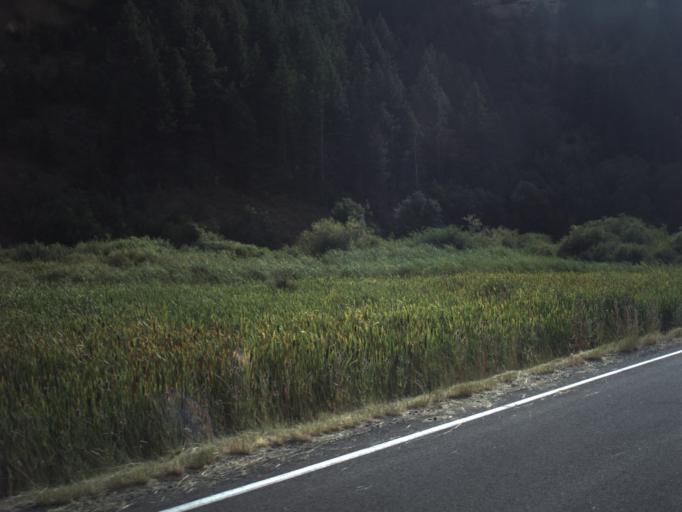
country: US
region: Utah
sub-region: Cache County
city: Millville
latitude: 41.6230
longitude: -111.6657
